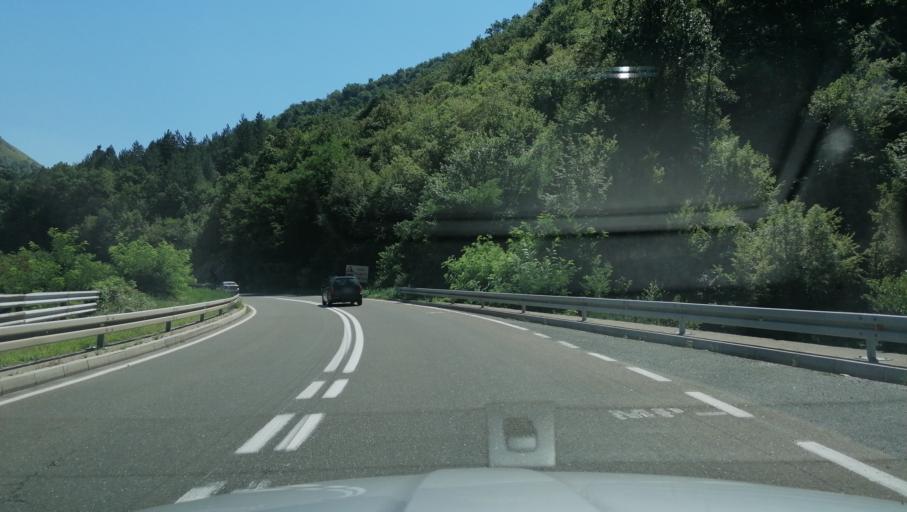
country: RS
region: Central Serbia
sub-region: Raski Okrug
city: Kraljevo
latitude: 43.5827
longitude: 20.5799
